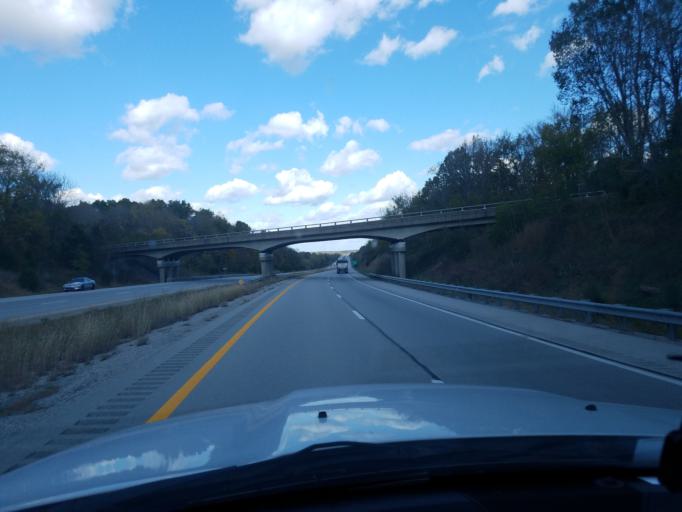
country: US
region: Kentucky
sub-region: Butler County
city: Morgantown
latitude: 37.2665
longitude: -86.7483
